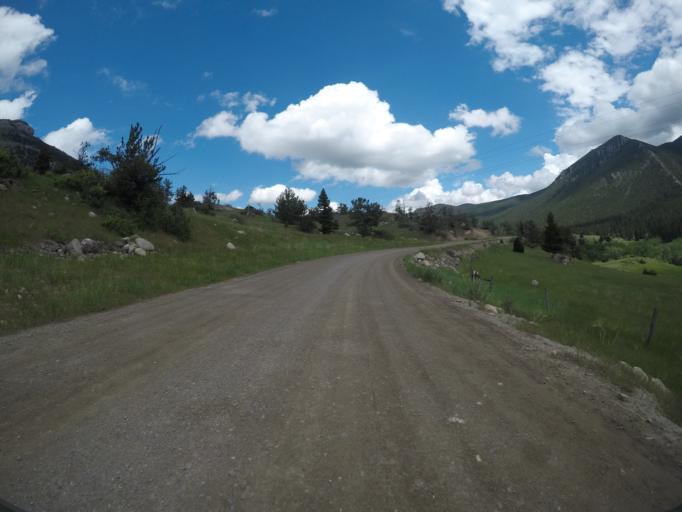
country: US
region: Montana
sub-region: Park County
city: Livingston
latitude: 45.5243
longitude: -110.2234
